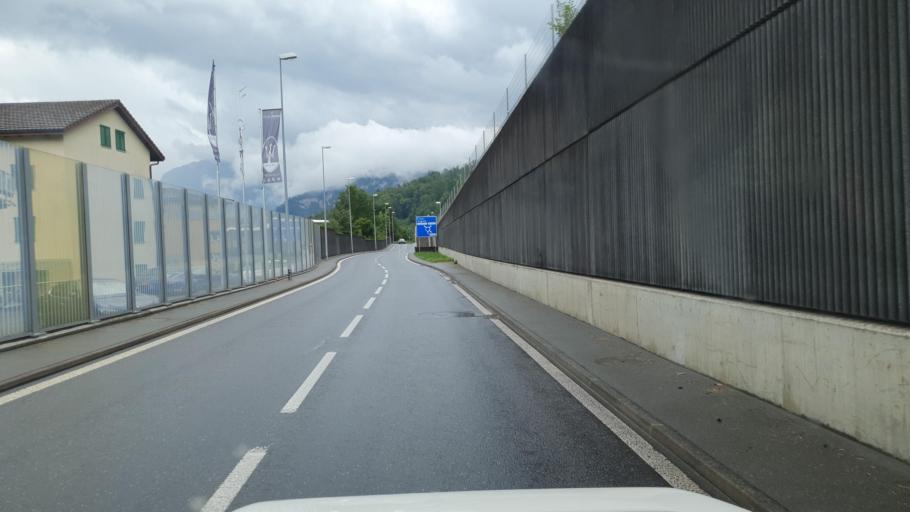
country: CH
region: Lucerne
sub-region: Lucerne-Land District
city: Horw
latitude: 47.0105
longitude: 8.3041
